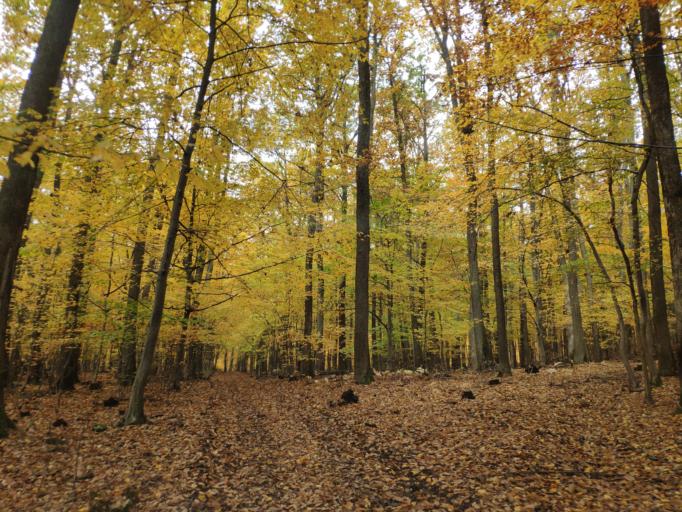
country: SK
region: Kosicky
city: Medzev
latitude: 48.7237
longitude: 20.9881
